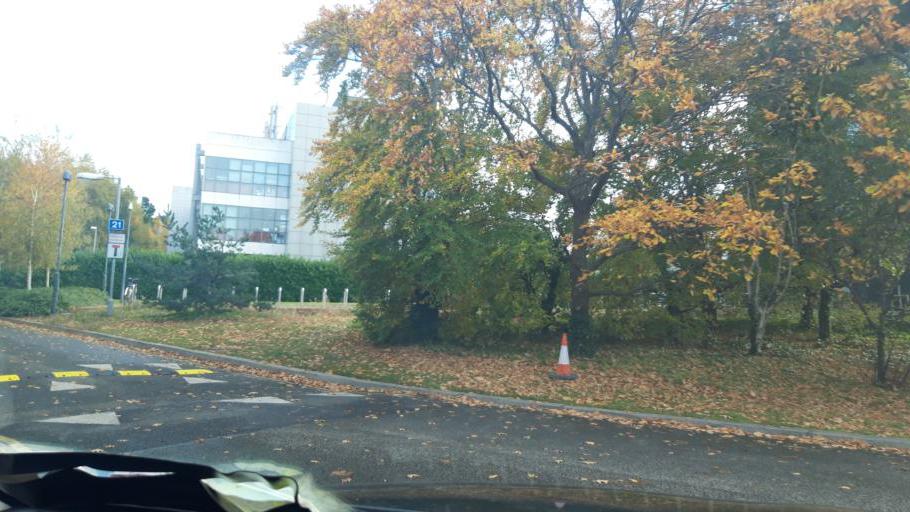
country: IE
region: Leinster
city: Donnybrook
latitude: 53.3105
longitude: -6.2267
